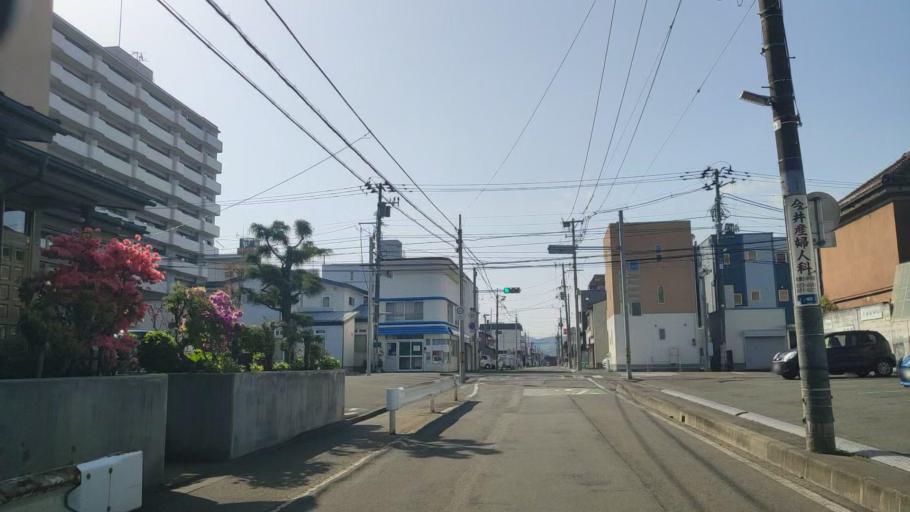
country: JP
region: Iwate
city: Morioka-shi
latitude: 39.6979
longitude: 141.1521
